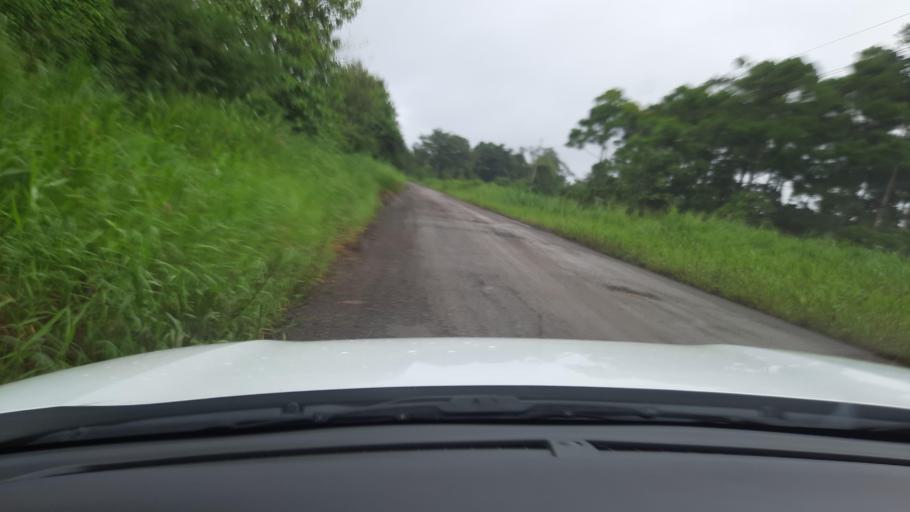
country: CR
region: Alajuela
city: San Jose
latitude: 11.0078
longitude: -85.3228
